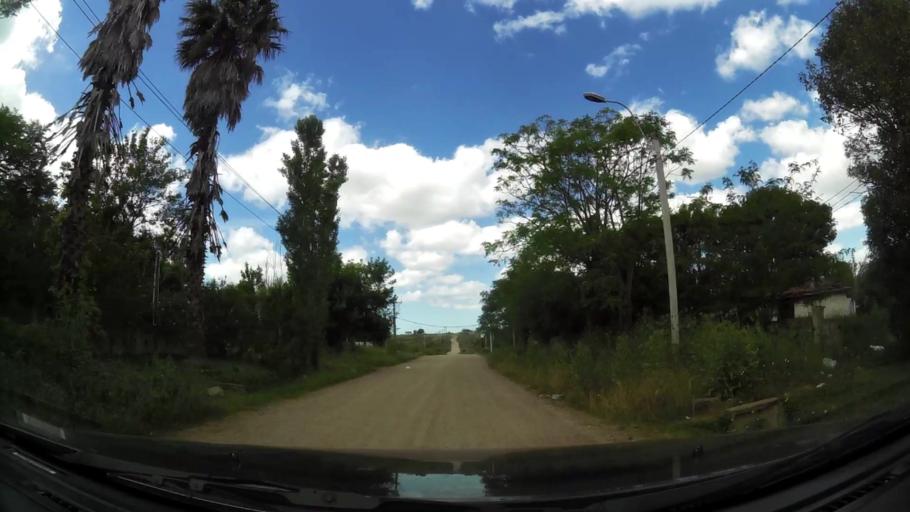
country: UY
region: Canelones
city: Colonia Nicolich
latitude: -34.8146
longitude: -56.0453
